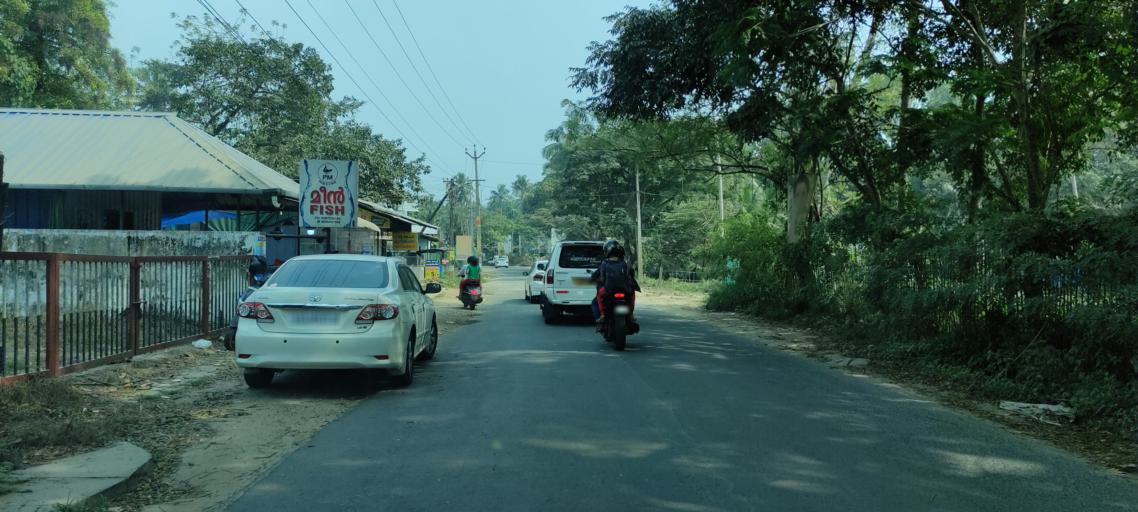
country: IN
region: Kerala
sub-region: Alappuzha
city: Shertallai
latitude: 9.6714
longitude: 76.4116
